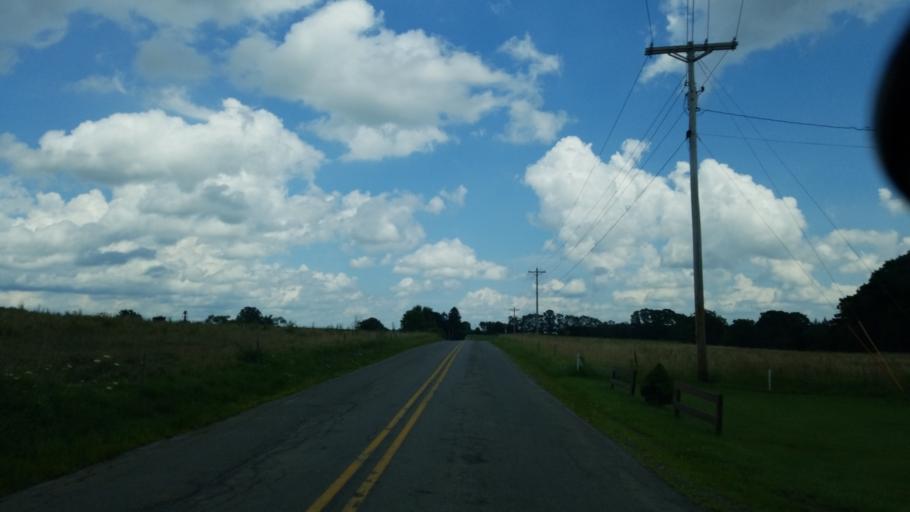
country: US
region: Pennsylvania
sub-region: Jefferson County
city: Brookville
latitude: 41.2390
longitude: -79.0358
